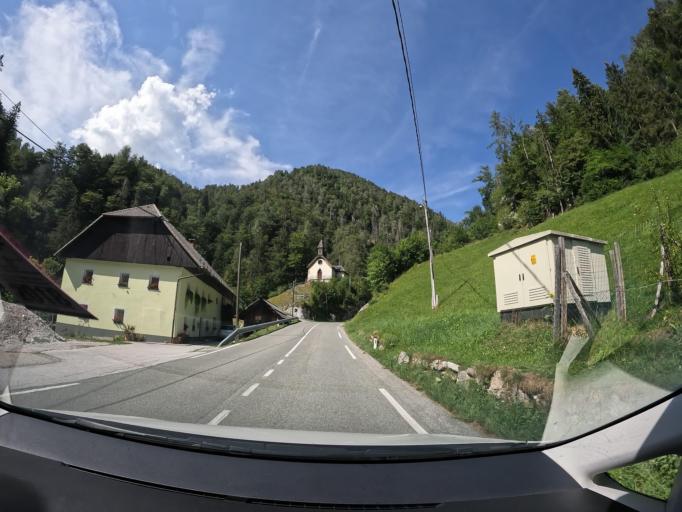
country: SI
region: Trzic
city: Trzic
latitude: 46.4114
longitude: 14.3001
